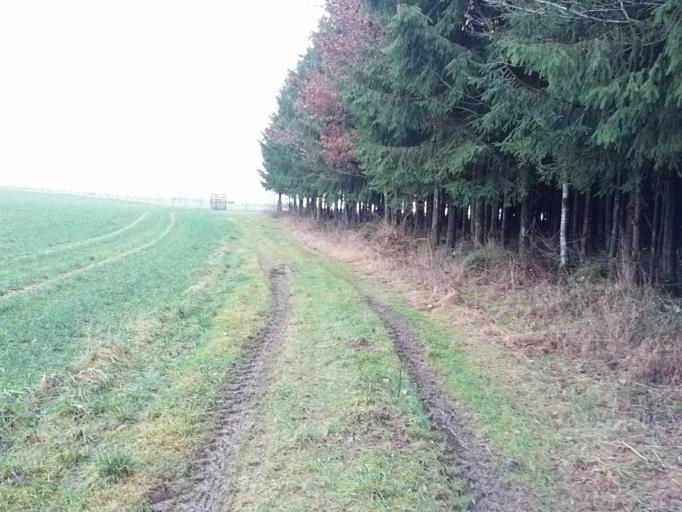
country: DE
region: Baden-Wuerttemberg
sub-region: Tuebingen Region
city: Steinhausen an der Rottum
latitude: 47.9836
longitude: 9.9754
